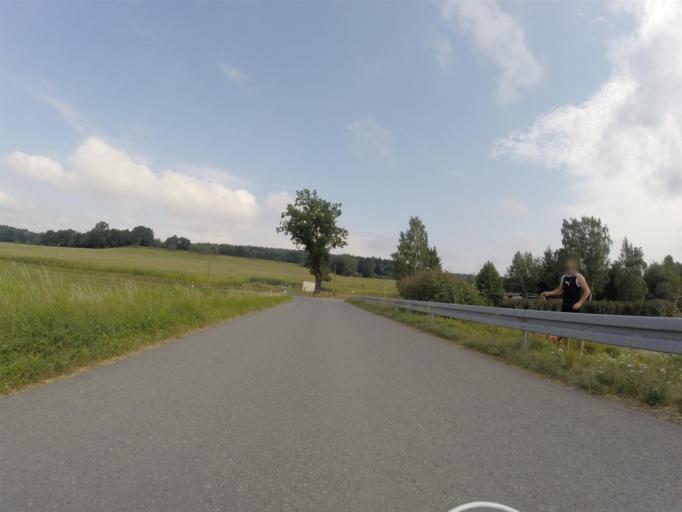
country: DE
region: Thuringia
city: Ruttersdorf-Lotschen
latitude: 50.8862
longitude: 11.7300
